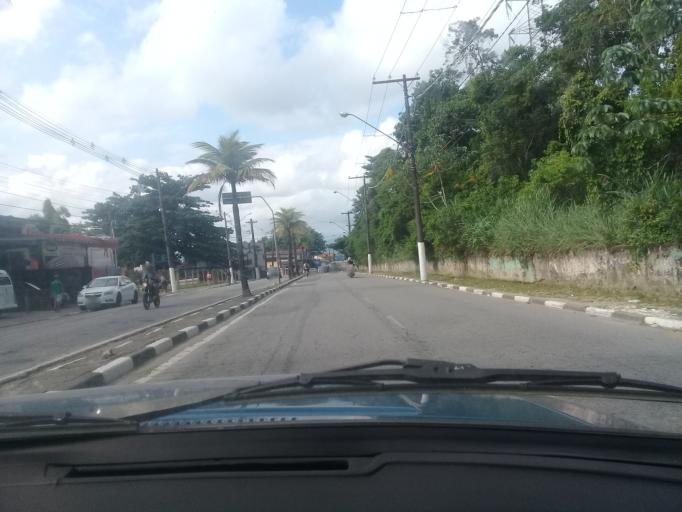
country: BR
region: Sao Paulo
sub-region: Guaruja
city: Guaruja
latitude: -23.9985
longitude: -46.2742
